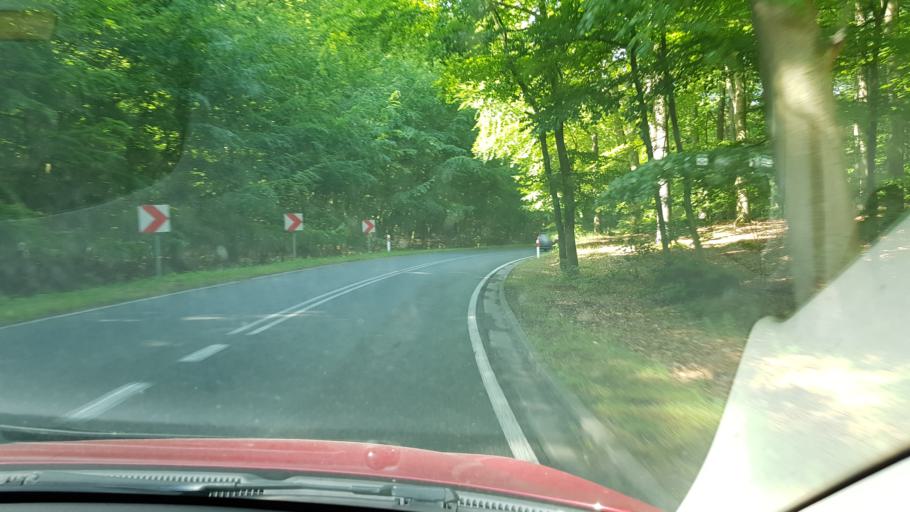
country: PL
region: West Pomeranian Voivodeship
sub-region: Powiat kamienski
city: Miedzyzdroje
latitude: 53.9561
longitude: 14.5002
